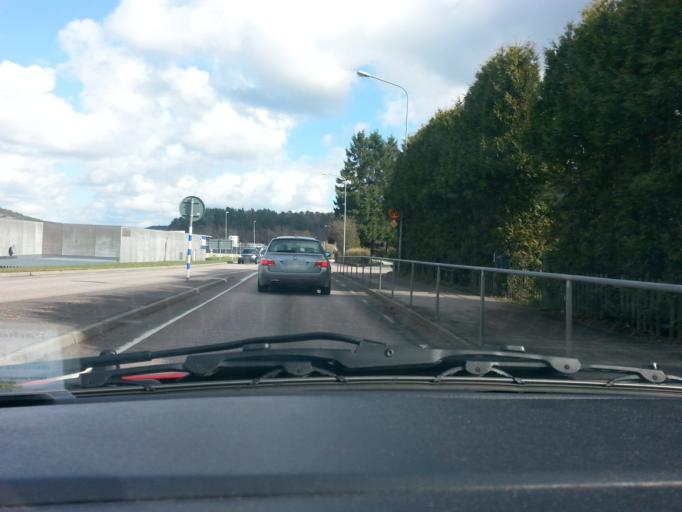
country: SE
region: Vaestra Goetaland
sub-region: Partille Kommun
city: Furulund
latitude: 57.7389
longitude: 12.1297
